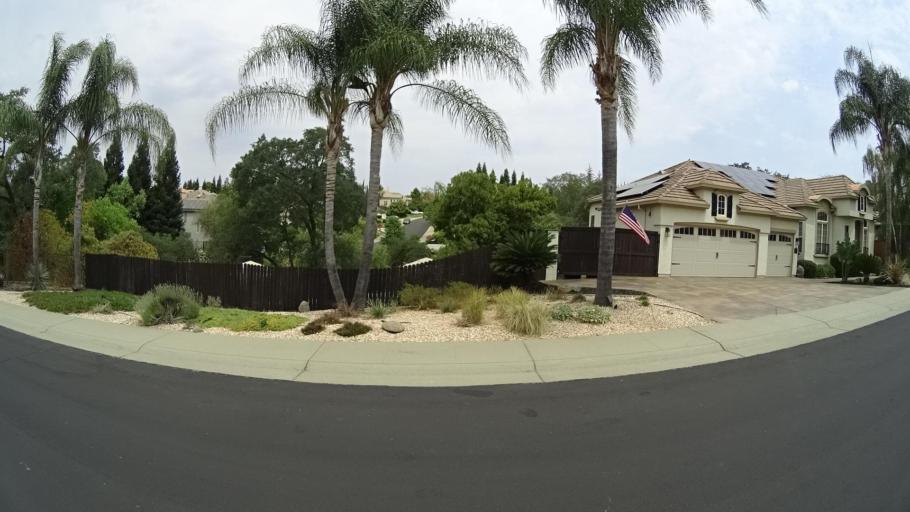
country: US
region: California
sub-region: Placer County
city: Rocklin
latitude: 38.7745
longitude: -121.2190
